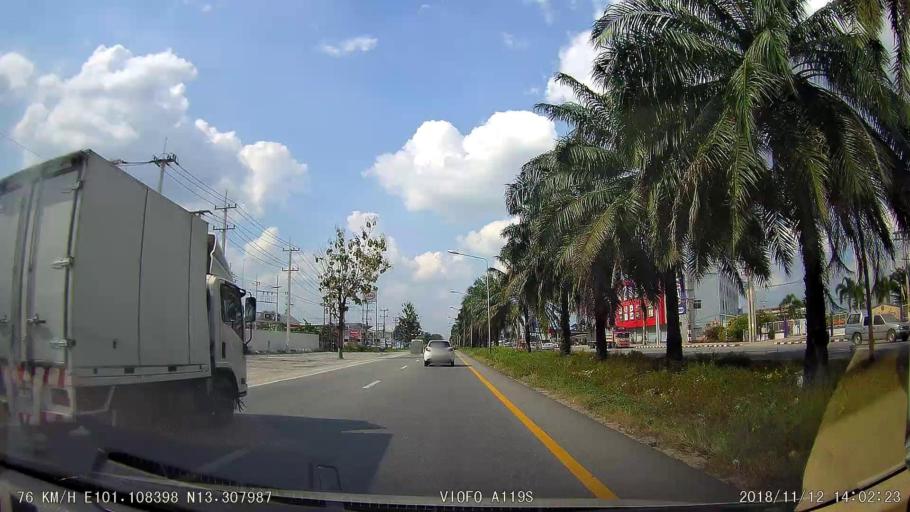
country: TH
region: Chon Buri
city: Ban Bueng
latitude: 13.3109
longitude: 101.1069
